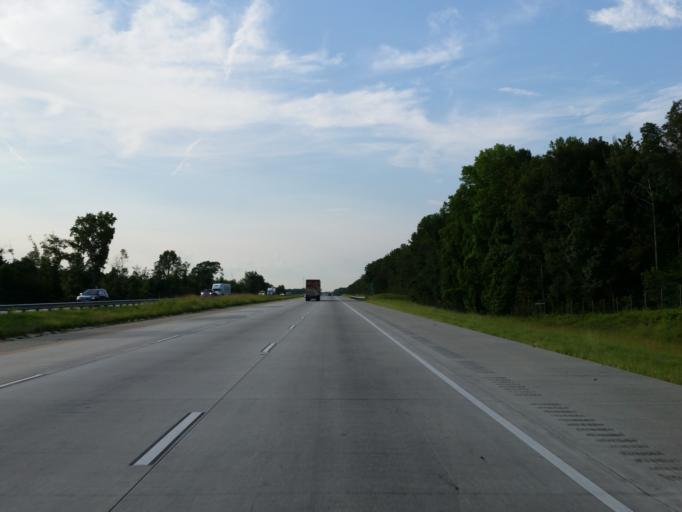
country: US
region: Georgia
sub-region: Dooly County
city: Unadilla
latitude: 32.3084
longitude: -83.7626
